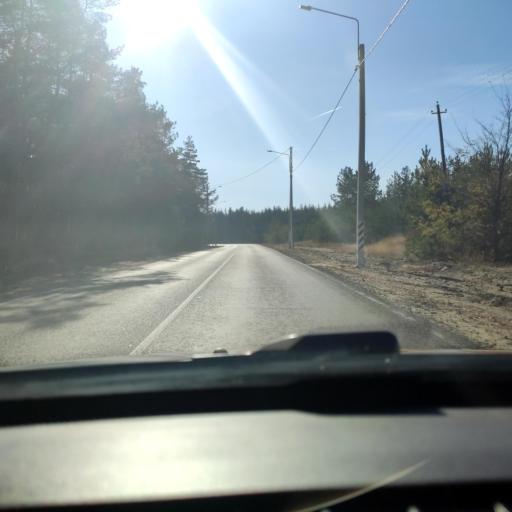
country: RU
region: Voronezj
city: Shilovo
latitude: 51.5308
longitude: 39.1407
